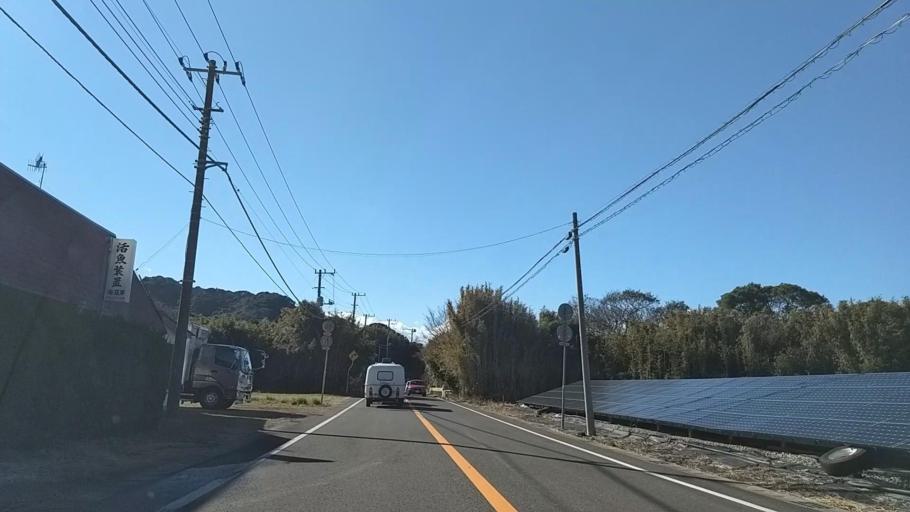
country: JP
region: Chiba
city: Tateyama
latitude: 34.9277
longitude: 139.8357
